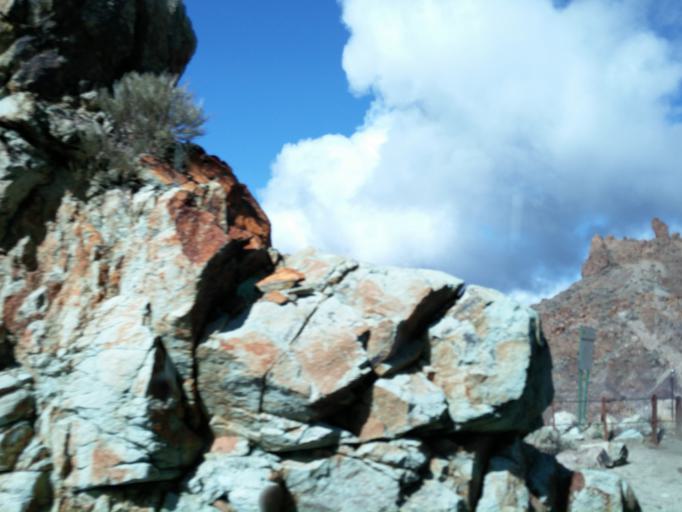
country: ES
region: Canary Islands
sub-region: Provincia de Santa Cruz de Tenerife
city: Vilaflor
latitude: 28.2184
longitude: -16.6278
